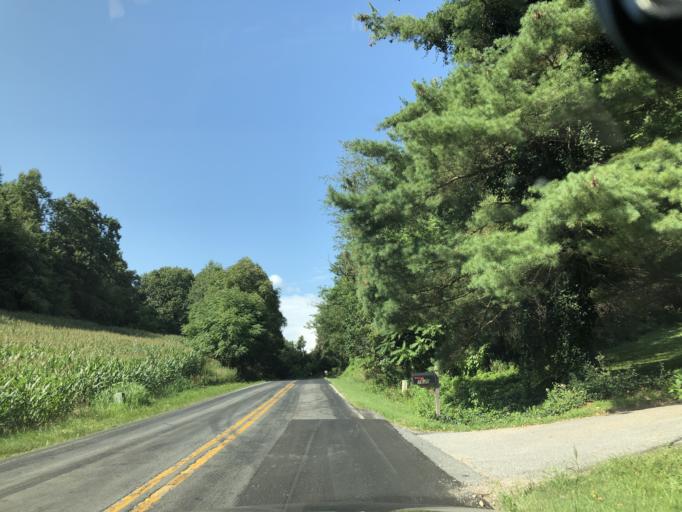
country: US
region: Maryland
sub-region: Frederick County
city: Linganore
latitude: 39.4443
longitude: -77.1761
